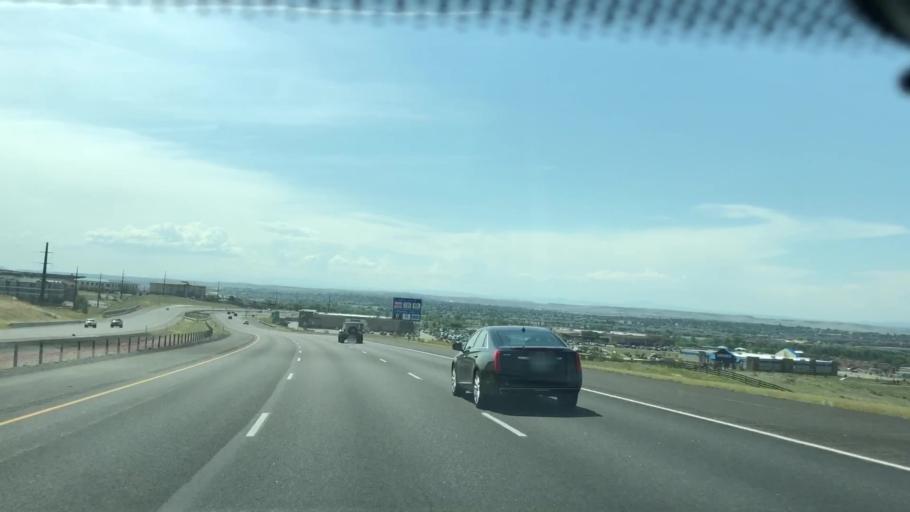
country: US
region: Colorado
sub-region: Douglas County
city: Parker
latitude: 39.5617
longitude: -104.7699
